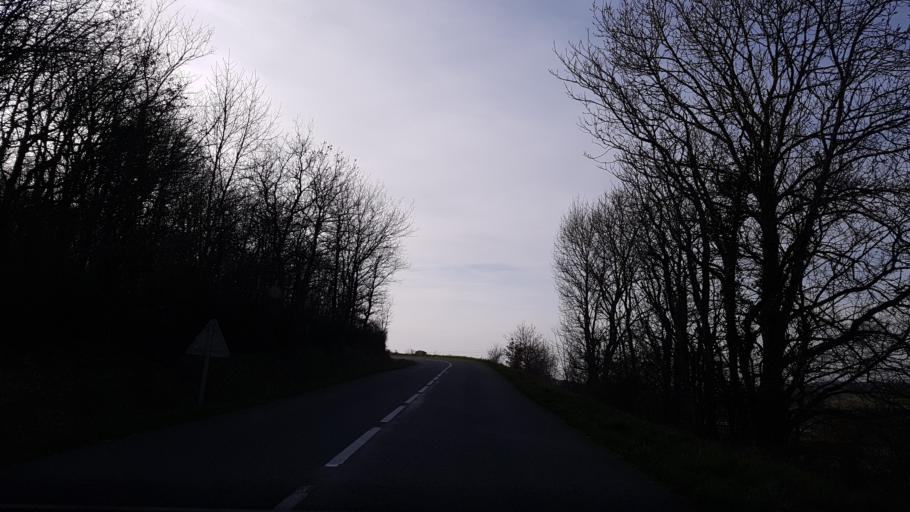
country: FR
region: Languedoc-Roussillon
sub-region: Departement de l'Aude
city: Villeneuve-la-Comptal
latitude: 43.2411
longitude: 1.9183
